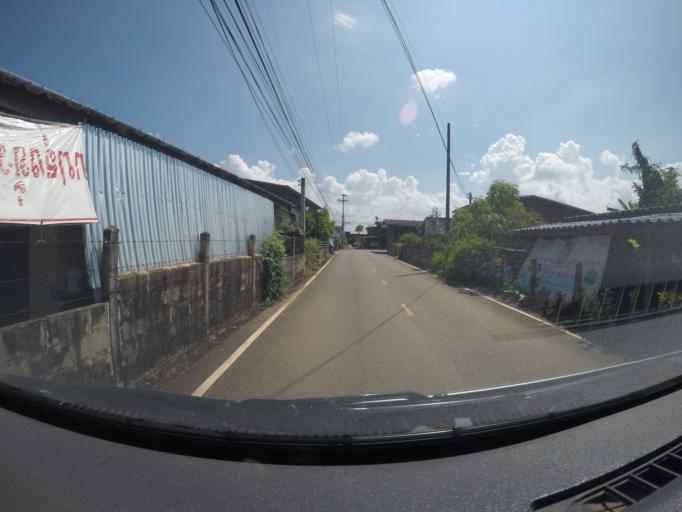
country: TH
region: Sakon Nakhon
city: Sakon Nakhon
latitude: 17.2103
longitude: 104.1333
